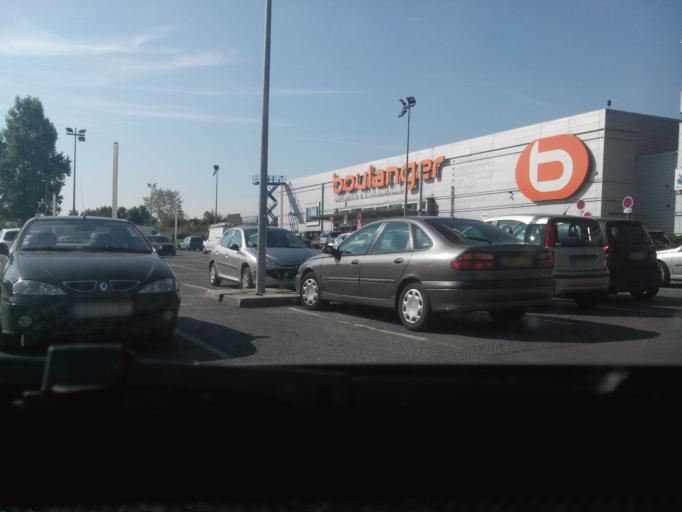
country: FR
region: Ile-de-France
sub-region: Departement de Seine-et-Marne
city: Lognes
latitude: 48.8327
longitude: 2.6413
